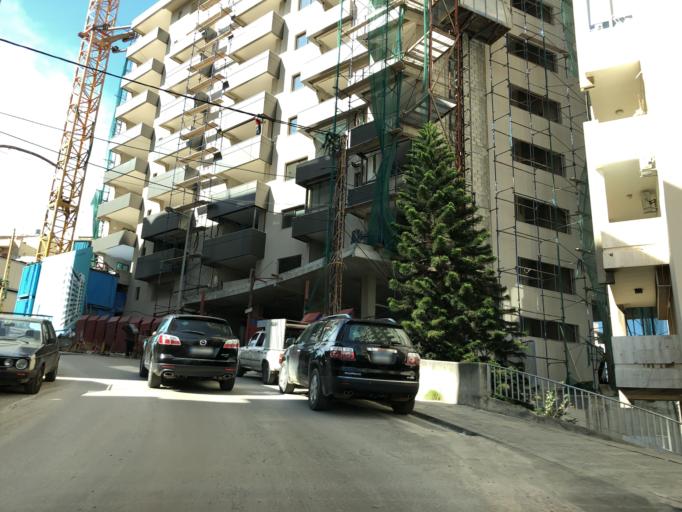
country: LB
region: Mont-Liban
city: Jdaidet el Matn
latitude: 33.8869
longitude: 35.5312
